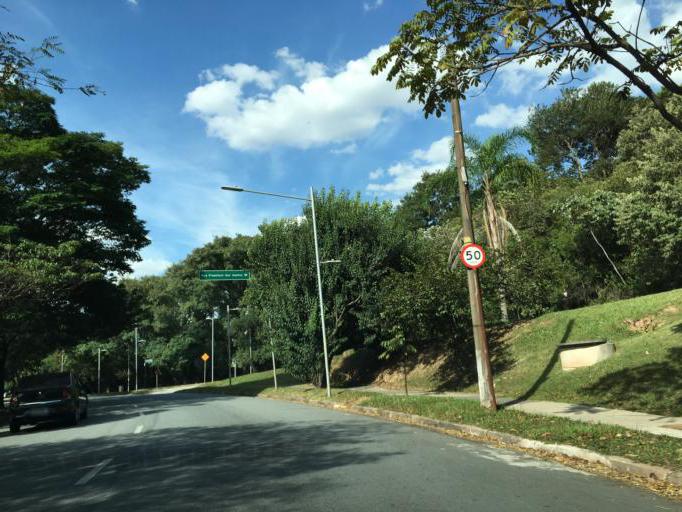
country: BR
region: Sao Paulo
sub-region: Osasco
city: Osasco
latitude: -23.5693
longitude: -46.7337
